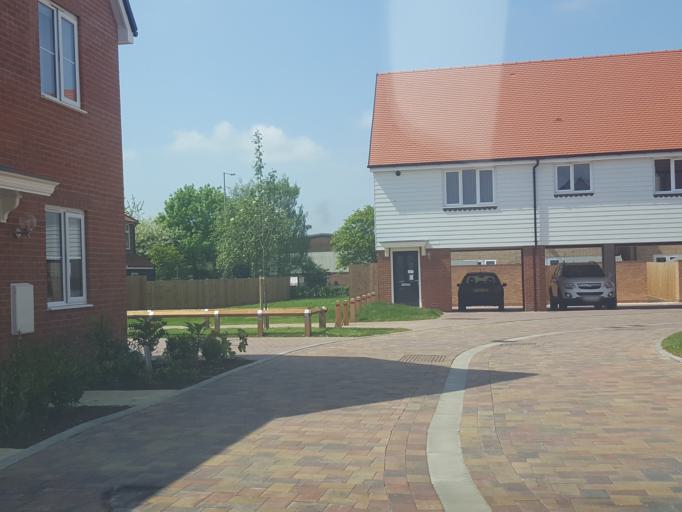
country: GB
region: England
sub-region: Essex
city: Colchester
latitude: 51.9158
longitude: 0.9316
